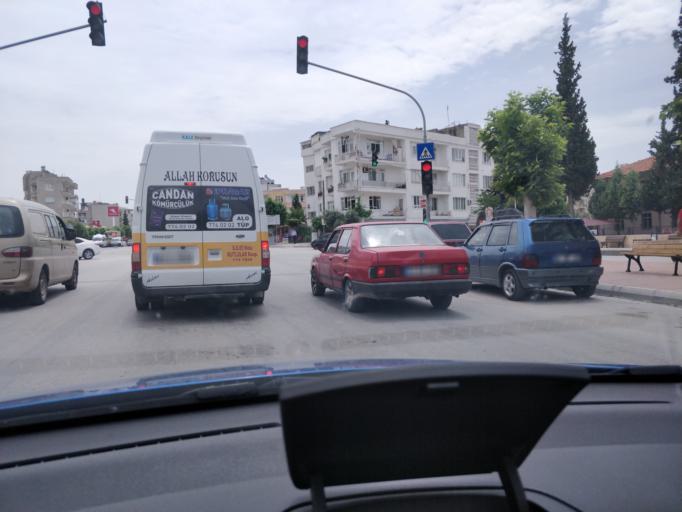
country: TR
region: Mersin
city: Mut
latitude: 36.6428
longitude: 33.4398
